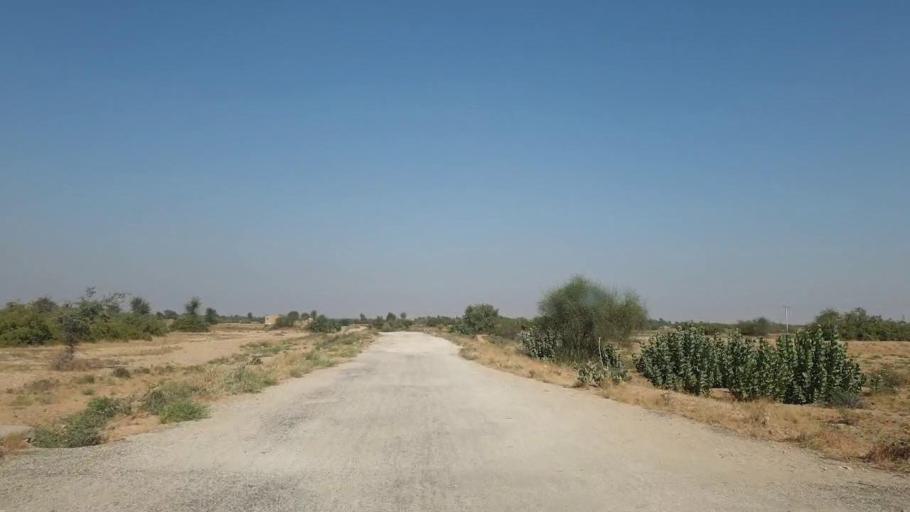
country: PK
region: Sindh
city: Jamshoro
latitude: 25.3862
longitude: 67.8469
